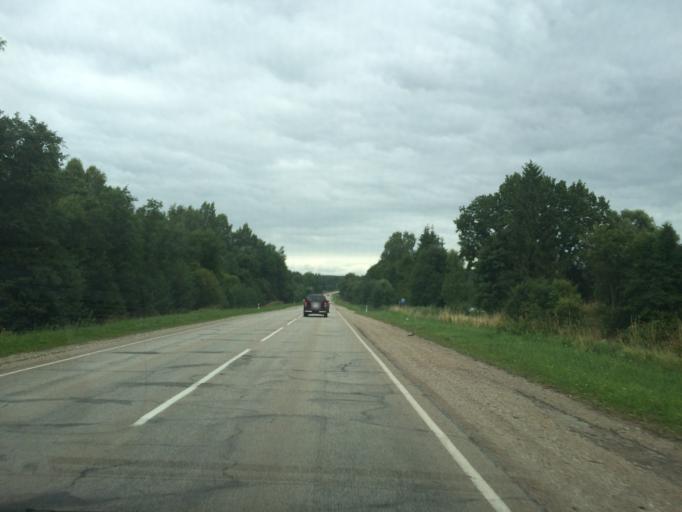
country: LV
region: Rezekne
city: Rezekne
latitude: 56.5617
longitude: 27.3648
